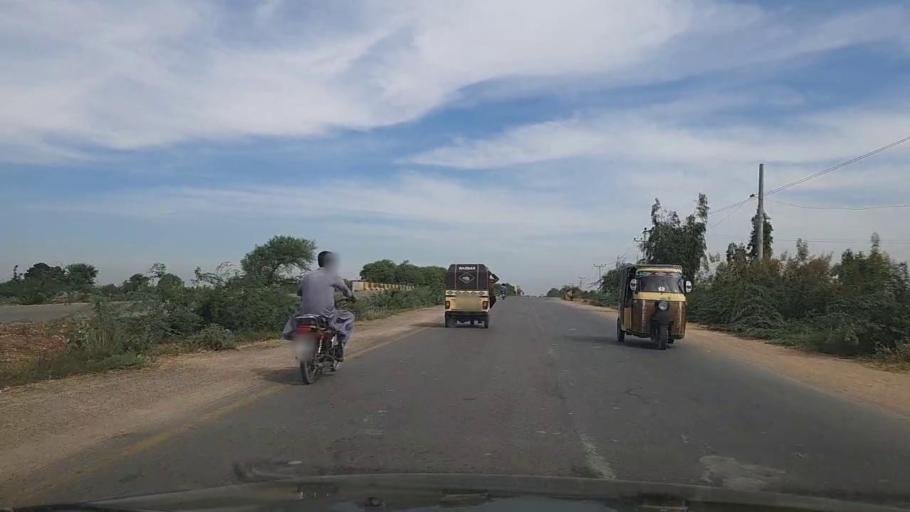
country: PK
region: Sindh
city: Thatta
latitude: 24.7652
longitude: 67.9361
